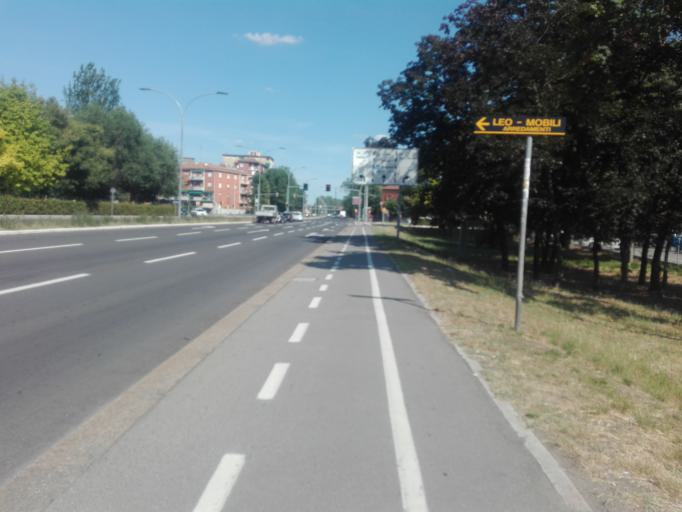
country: IT
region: Emilia-Romagna
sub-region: Provincia di Bologna
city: Casalecchio di Reno
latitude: 44.5030
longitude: 11.2967
